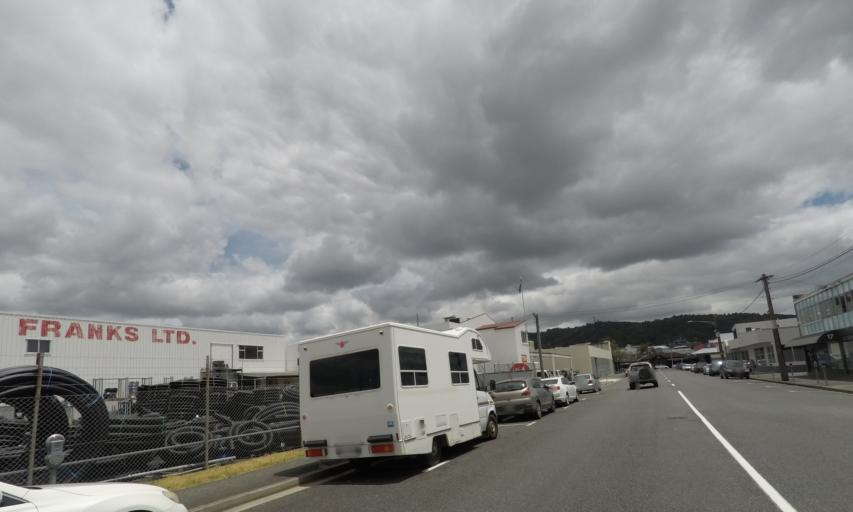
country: NZ
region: Northland
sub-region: Whangarei
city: Whangarei
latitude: -35.7270
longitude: 174.3240
